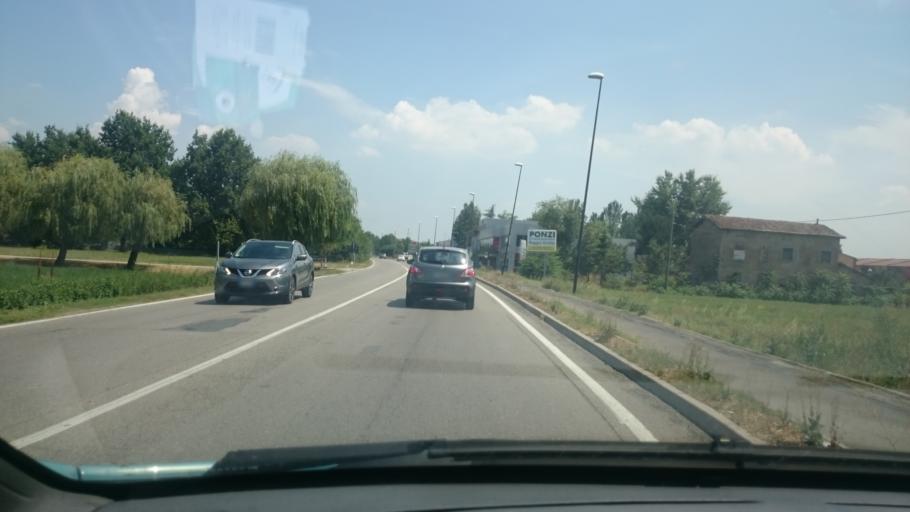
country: IT
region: Emilia-Romagna
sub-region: Provincia di Reggio Emilia
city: Bagno
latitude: 44.6580
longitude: 10.7479
